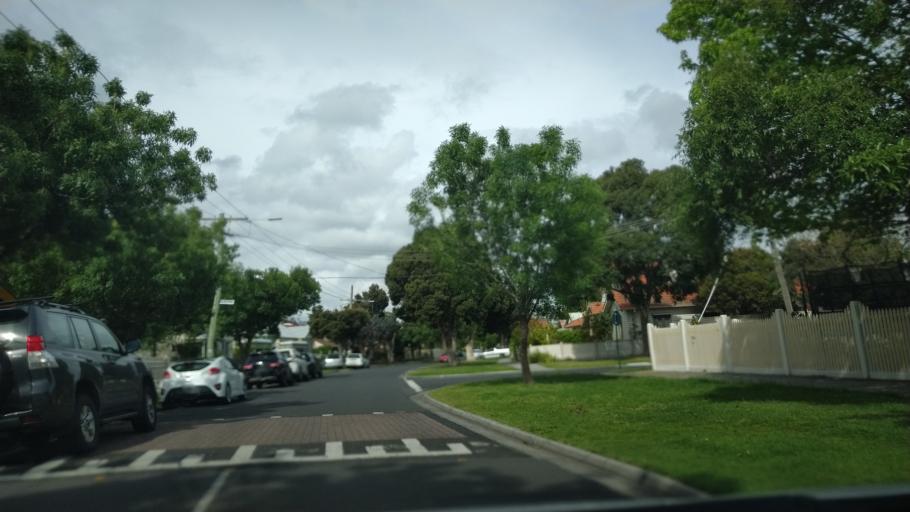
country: AU
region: Victoria
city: Hughesdale
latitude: -37.8970
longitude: 145.0802
